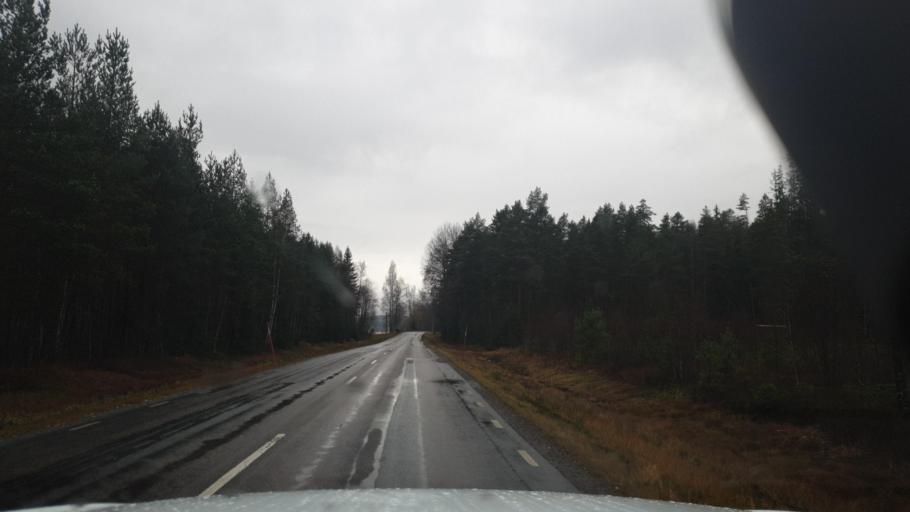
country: SE
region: Vaermland
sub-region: Eda Kommun
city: Charlottenberg
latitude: 59.8211
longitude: 12.2615
